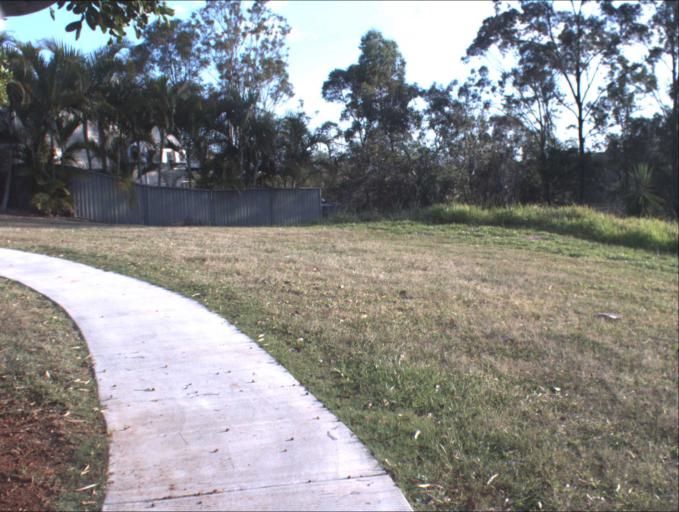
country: AU
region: Queensland
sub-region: Logan
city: Beenleigh
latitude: -27.6741
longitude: 153.1996
